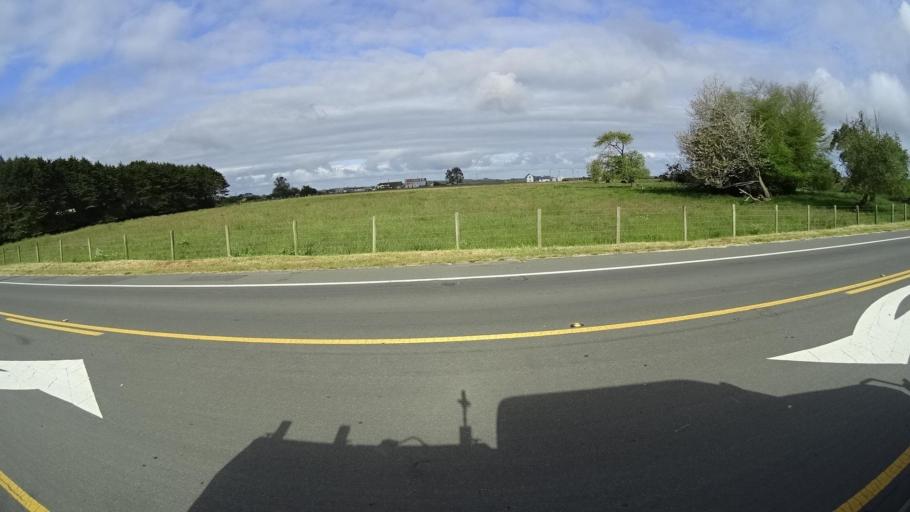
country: US
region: California
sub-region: Humboldt County
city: Arcata
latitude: 40.9020
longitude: -124.0913
